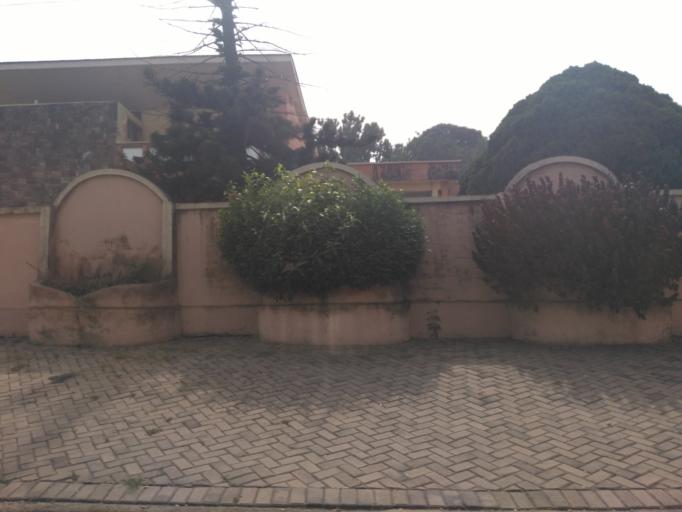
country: GH
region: Ashanti
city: Kumasi
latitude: 6.6791
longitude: -1.5993
